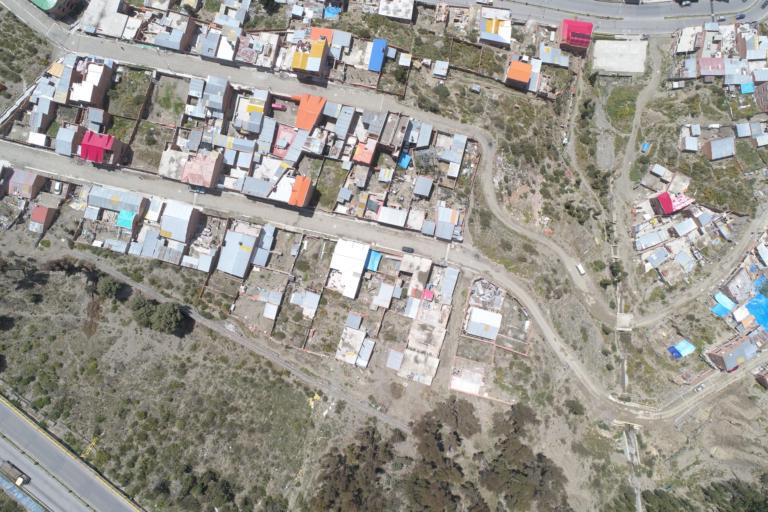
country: BO
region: La Paz
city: La Paz
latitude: -16.5334
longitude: -68.1470
